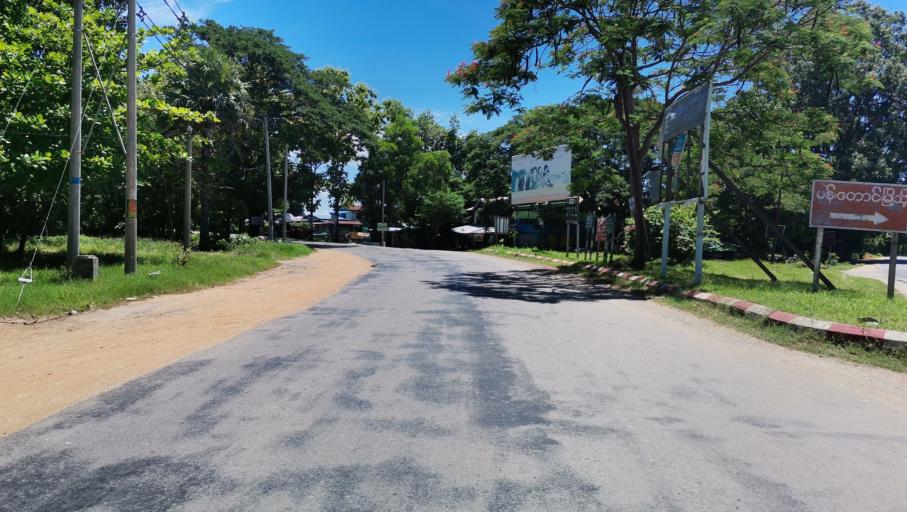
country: MM
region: Bago
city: Pyay
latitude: 18.6992
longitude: 95.0954
